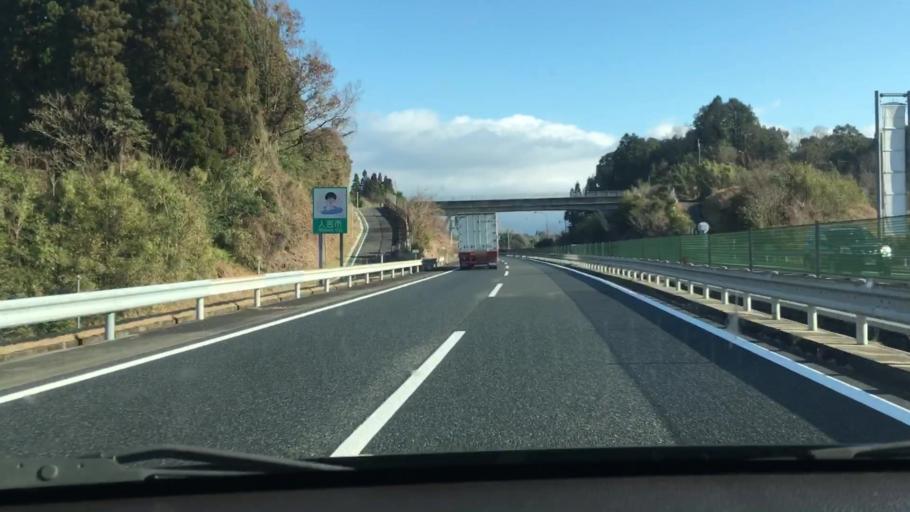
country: JP
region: Kumamoto
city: Hitoyoshi
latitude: 32.2344
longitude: 130.7660
